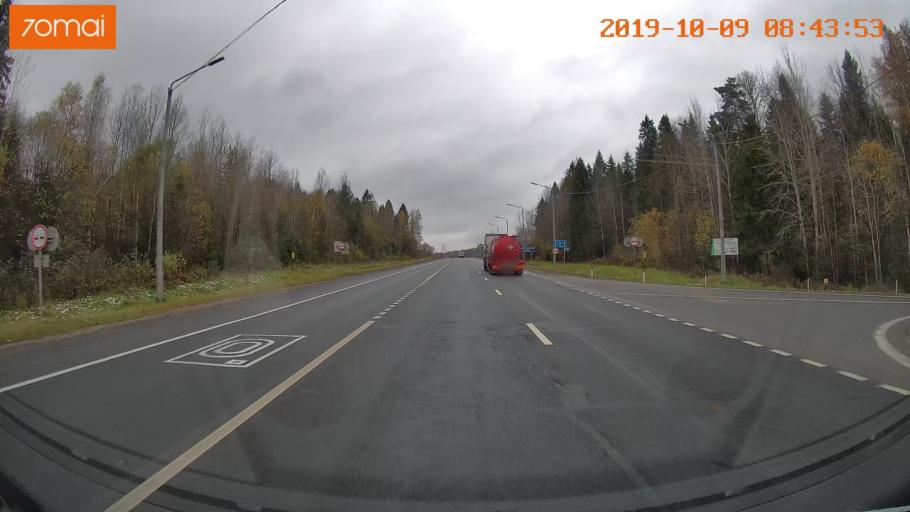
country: RU
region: Vologda
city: Gryazovets
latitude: 59.0288
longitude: 40.1120
